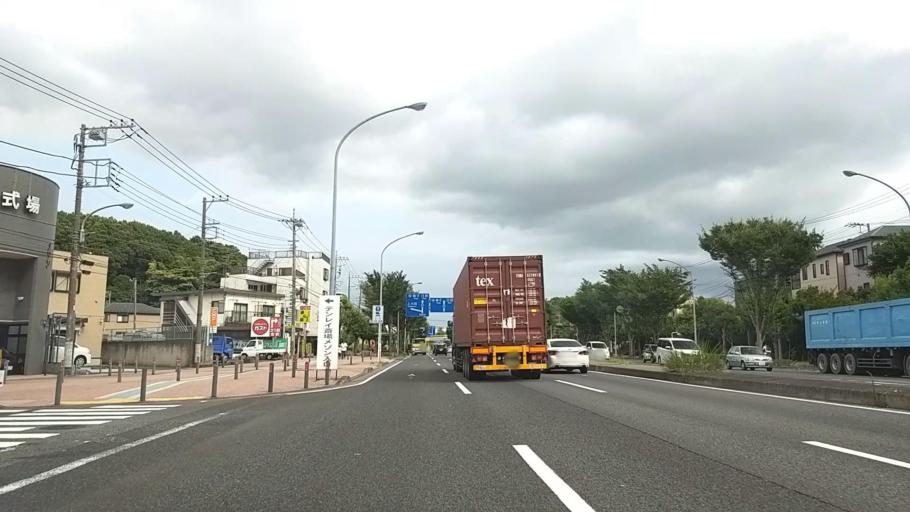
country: JP
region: Kanagawa
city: Yokohama
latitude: 35.4072
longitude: 139.5661
